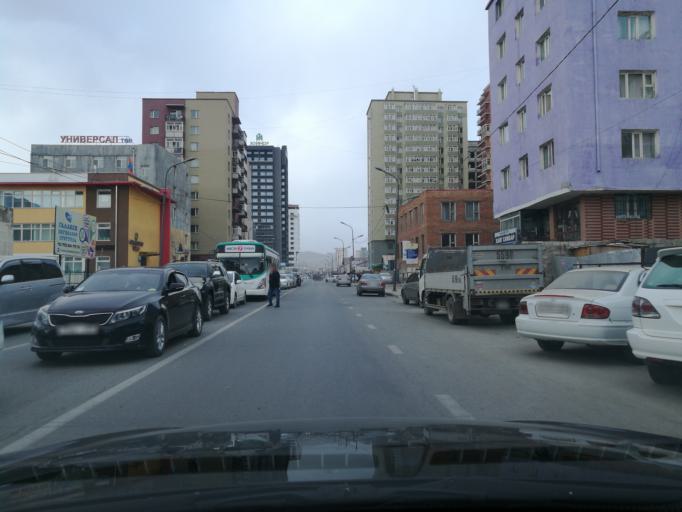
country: MN
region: Ulaanbaatar
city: Ulaanbaatar
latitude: 47.9298
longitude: 106.9142
